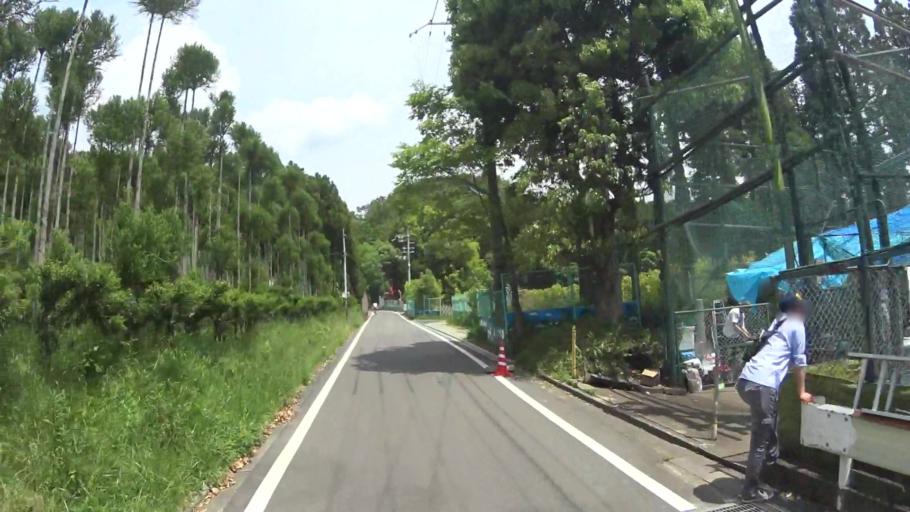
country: JP
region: Kyoto
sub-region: Kyoto-shi
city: Kamigyo-ku
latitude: 35.0558
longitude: 135.7292
